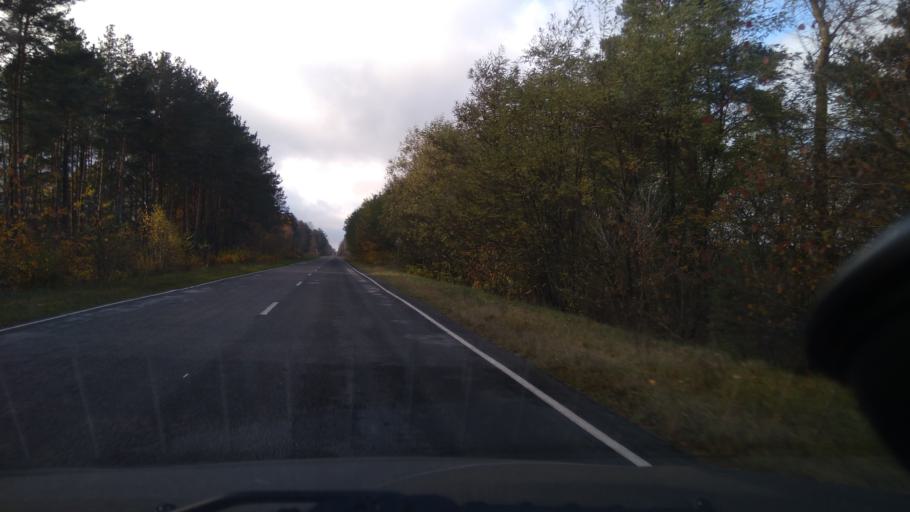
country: BY
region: Minsk
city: Urechcha
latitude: 53.2098
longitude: 27.9853
